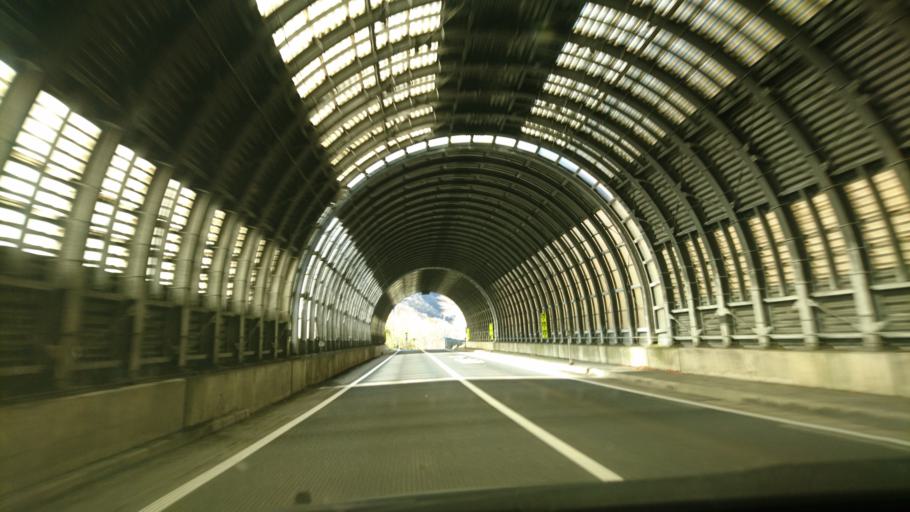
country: JP
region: Iwate
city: Kitakami
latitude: 39.2996
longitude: 140.9005
